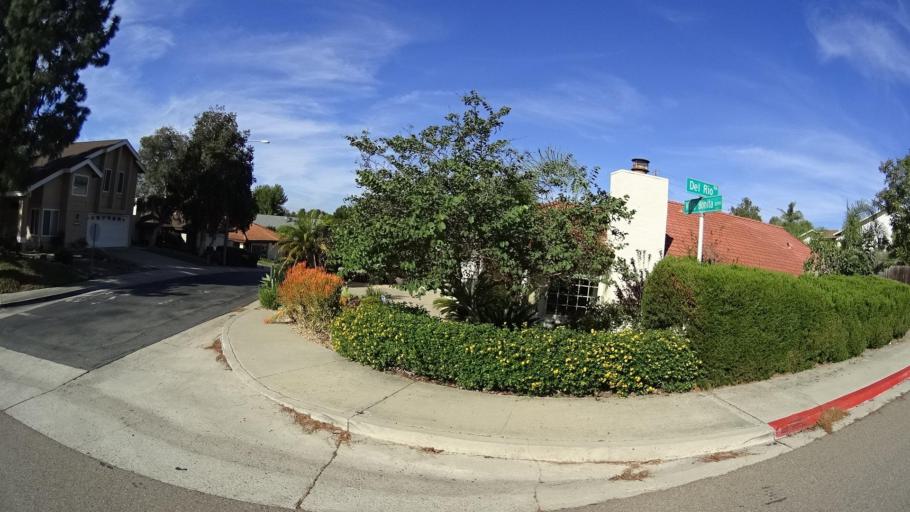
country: US
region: California
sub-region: San Diego County
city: Rancho San Diego
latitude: 32.7362
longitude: -116.9614
